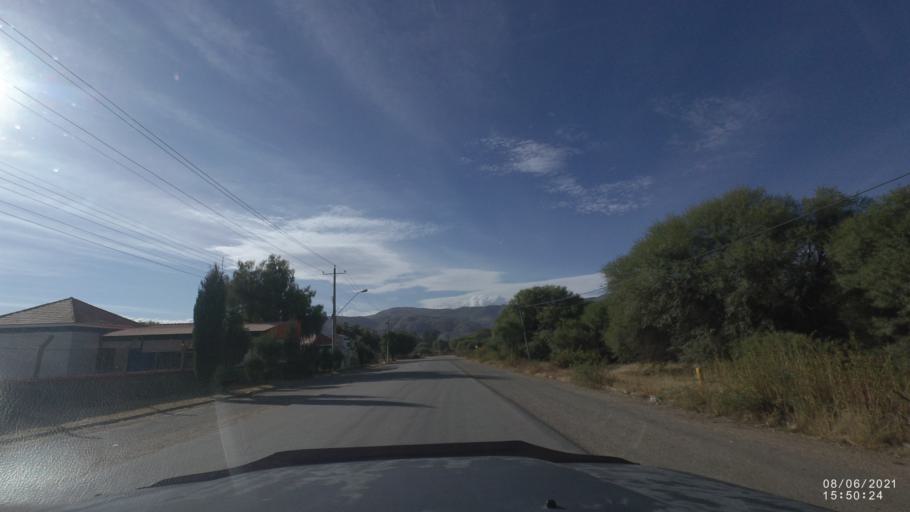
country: BO
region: Cochabamba
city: Capinota
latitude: -17.5573
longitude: -66.2501
